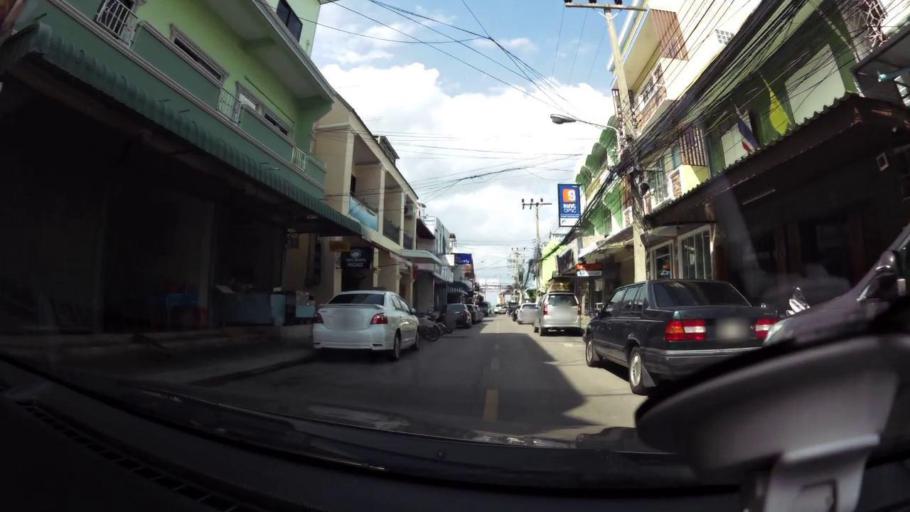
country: TH
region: Prachuap Khiri Khan
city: Hua Hin
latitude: 12.5724
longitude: 99.9590
